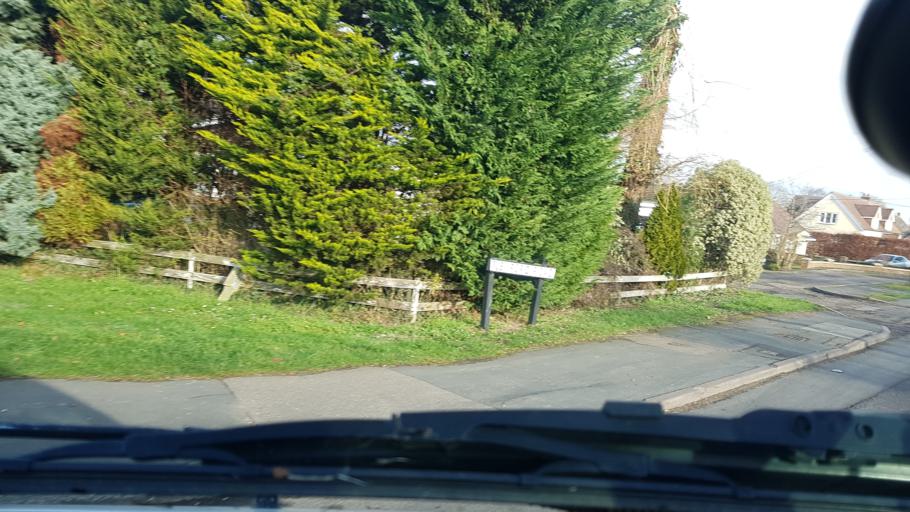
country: GB
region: England
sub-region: Surrey
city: Normandy
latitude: 51.2404
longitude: -0.6726
